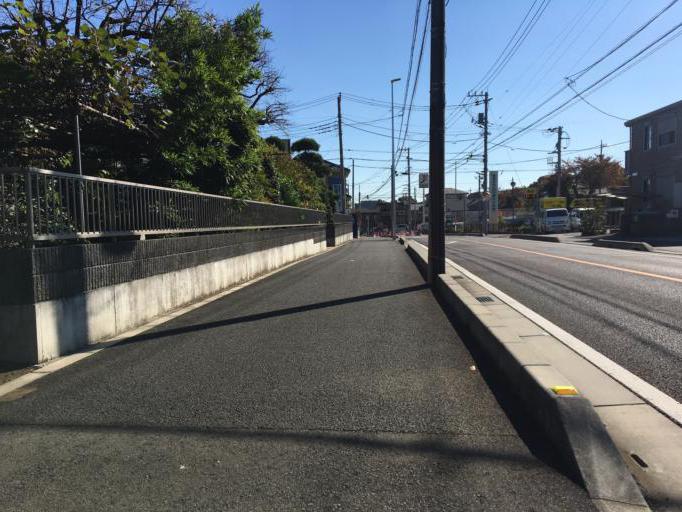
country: JP
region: Saitama
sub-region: Kawaguchi-shi
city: Hatogaya-honcho
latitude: 35.8416
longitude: 139.7362
